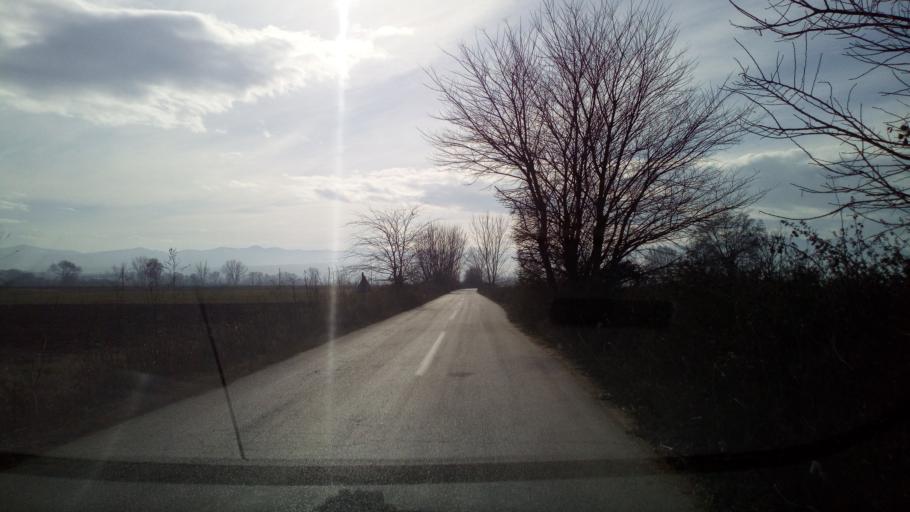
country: GR
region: Central Macedonia
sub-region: Nomos Thessalonikis
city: Gerakarou
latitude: 40.6538
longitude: 23.2483
